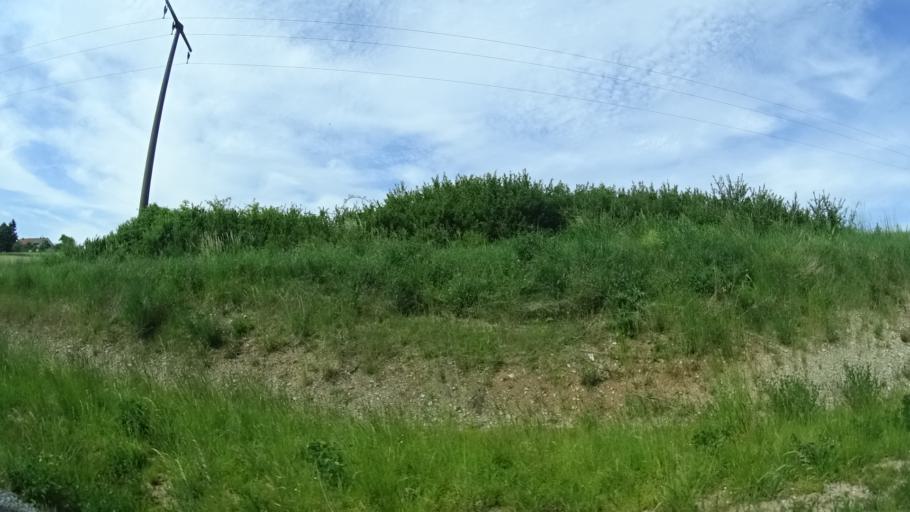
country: DE
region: Bavaria
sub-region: Regierungsbezirk Unterfranken
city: Birkenfeld
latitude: 49.8607
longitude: 9.6852
